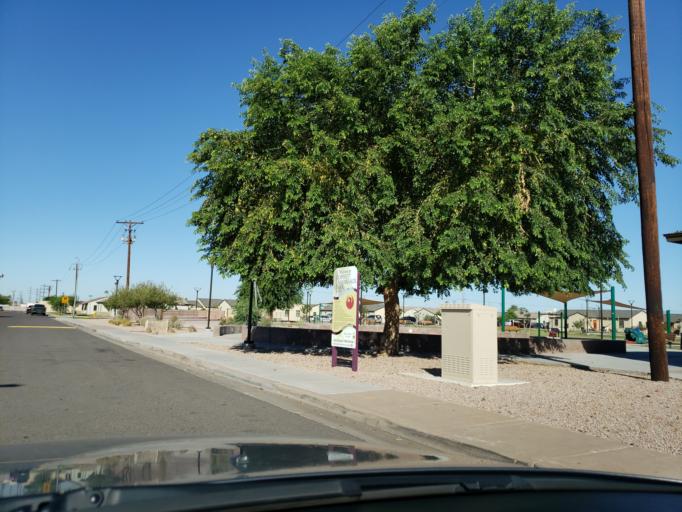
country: US
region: Arizona
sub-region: Maricopa County
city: Phoenix
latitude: 33.4331
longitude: -112.1012
